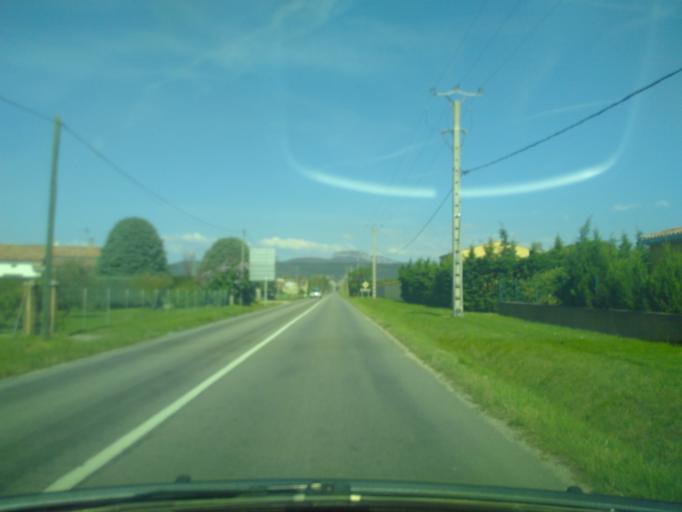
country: FR
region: Rhone-Alpes
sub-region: Departement de la Drome
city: La Begude-de-Mazenc
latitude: 44.6127
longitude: 4.9398
